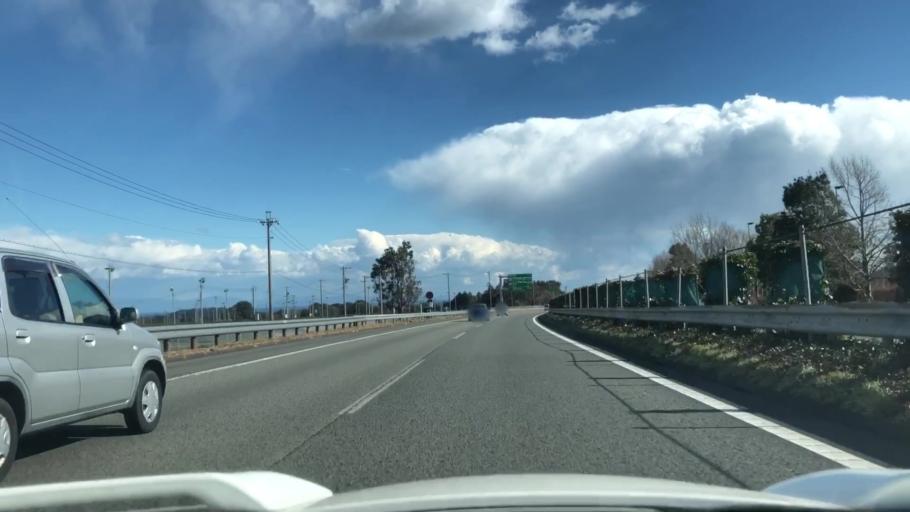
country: JP
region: Shizuoka
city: Shimada
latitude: 34.7589
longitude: 138.1652
